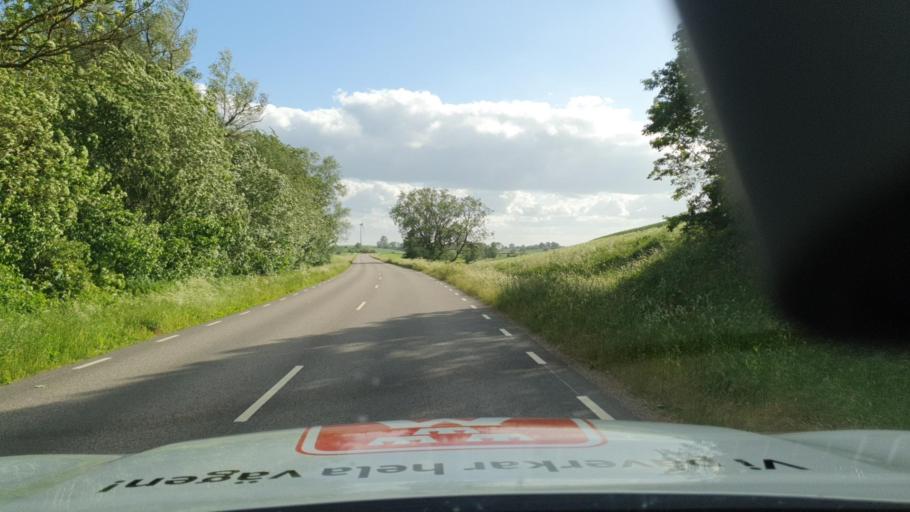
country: SE
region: Skane
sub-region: Tomelilla Kommun
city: Tomelilla
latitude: 55.5774
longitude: 14.0045
